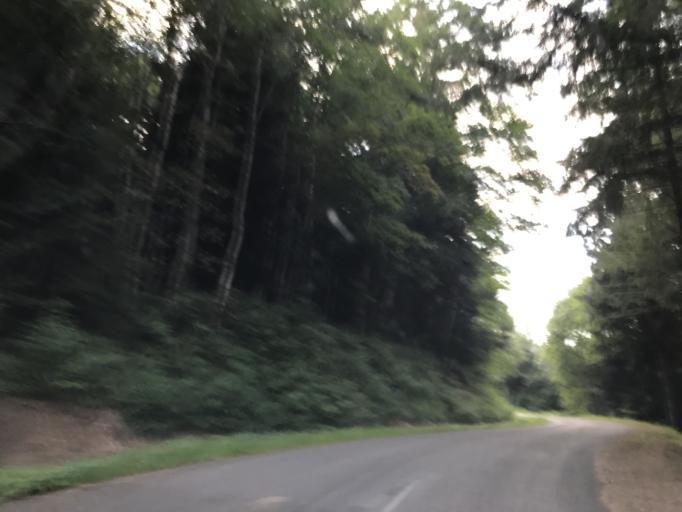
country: FR
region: Rhone-Alpes
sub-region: Departement de la Loire
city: Noiretable
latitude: 45.7753
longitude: 3.7863
